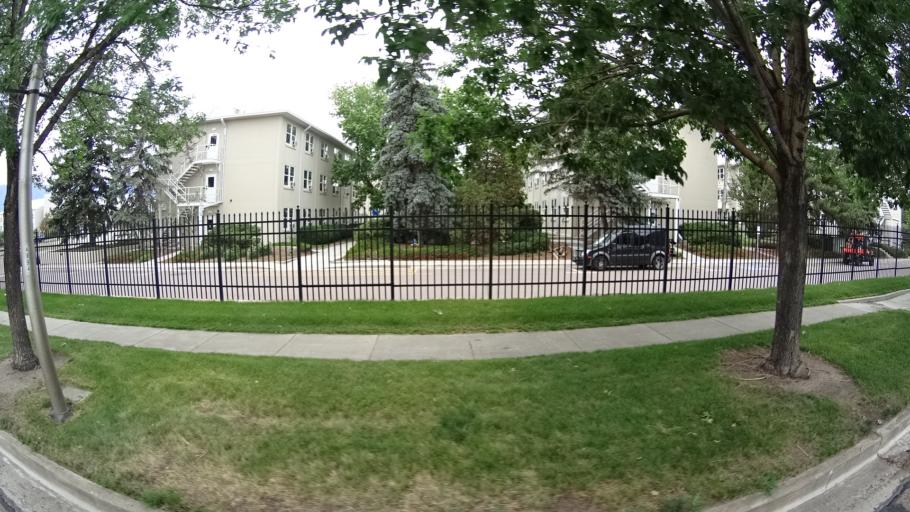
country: US
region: Colorado
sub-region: El Paso County
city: Colorado Springs
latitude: 38.8436
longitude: -104.7944
